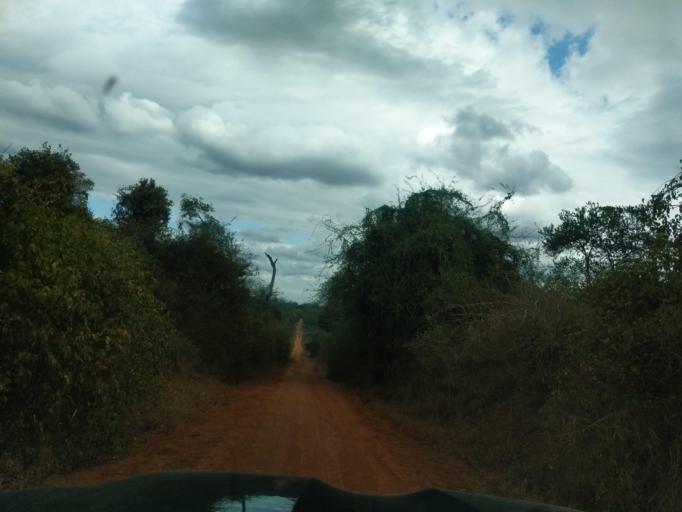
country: TZ
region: Pwani
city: Mvomero
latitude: -5.9338
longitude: 38.4202
